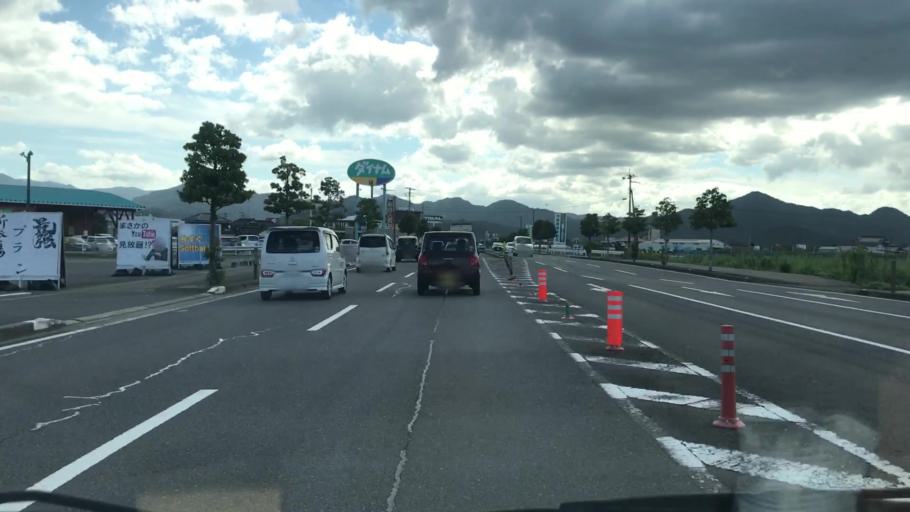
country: JP
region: Saga Prefecture
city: Kashima
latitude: 33.1256
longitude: 130.1006
